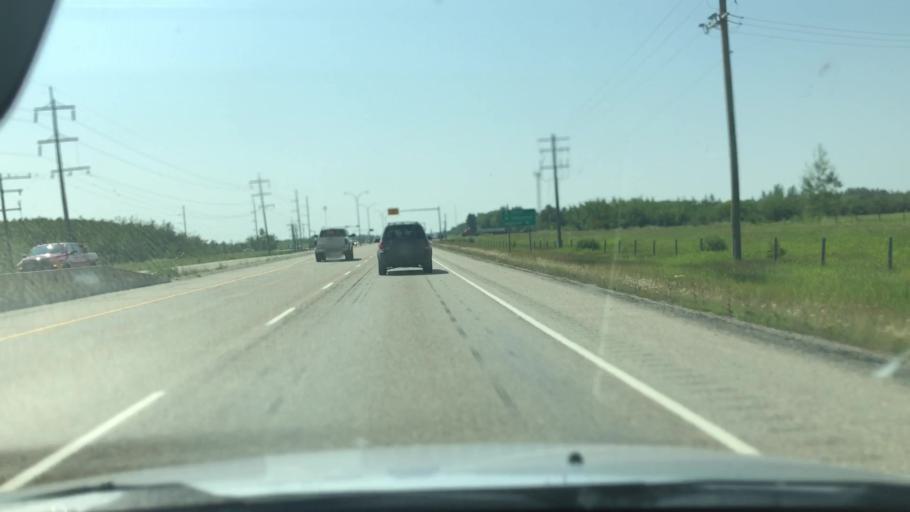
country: CA
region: Alberta
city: Devon
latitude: 53.4570
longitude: -113.7627
